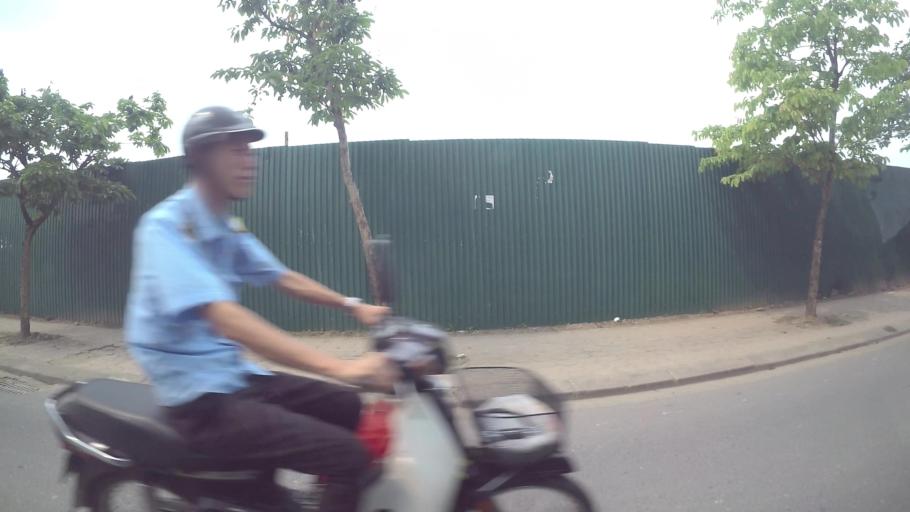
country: VN
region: Ha Noi
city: Trau Quy
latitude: 21.0374
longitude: 105.9323
